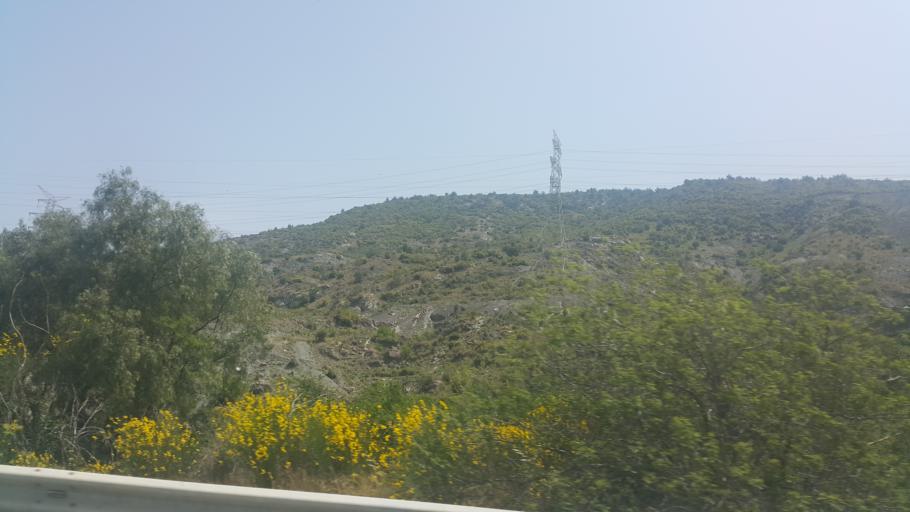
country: TR
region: Hatay
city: Guzelkoy
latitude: 36.5955
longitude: 36.2062
